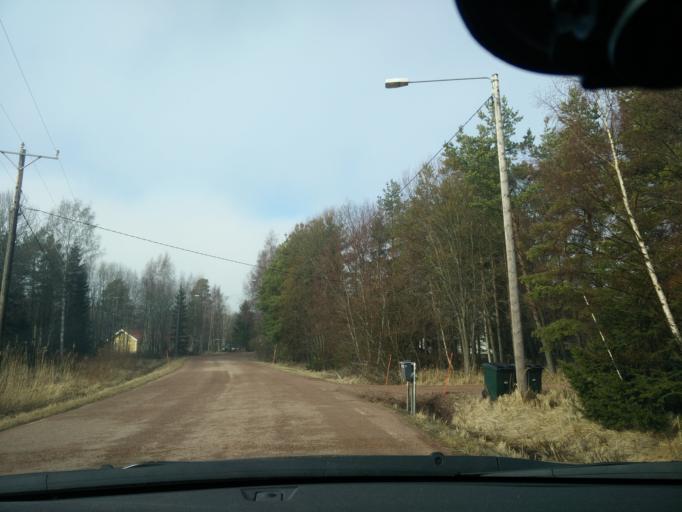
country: AX
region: Mariehamns stad
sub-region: Mariehamn
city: Mariehamn
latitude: 60.0994
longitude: 19.9079
